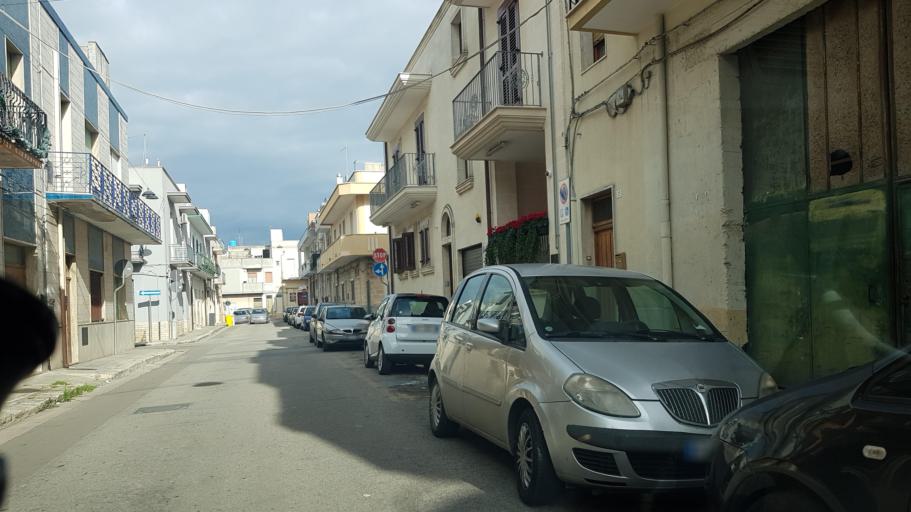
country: IT
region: Apulia
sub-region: Provincia di Brindisi
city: Francavilla Fontana
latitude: 40.5236
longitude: 17.5799
